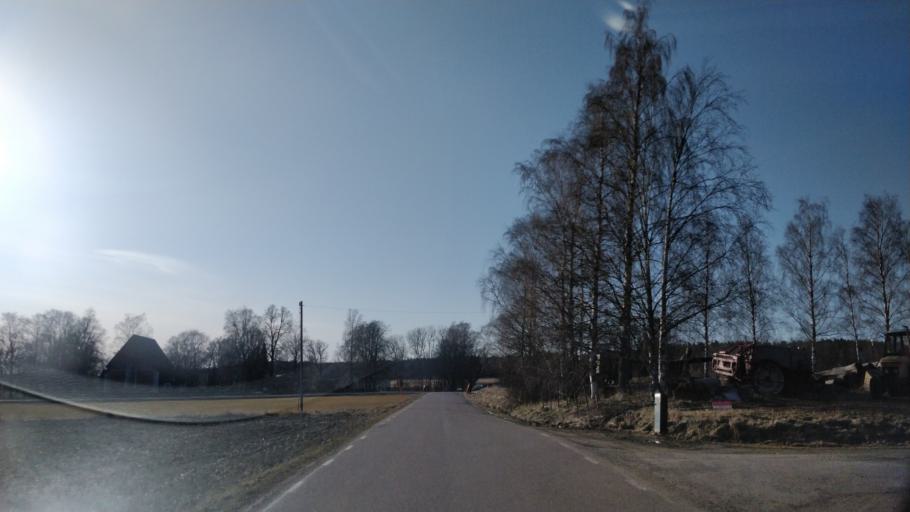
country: SE
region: Uppsala
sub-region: Enkopings Kommun
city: Orsundsbro
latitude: 59.7512
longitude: 17.1770
